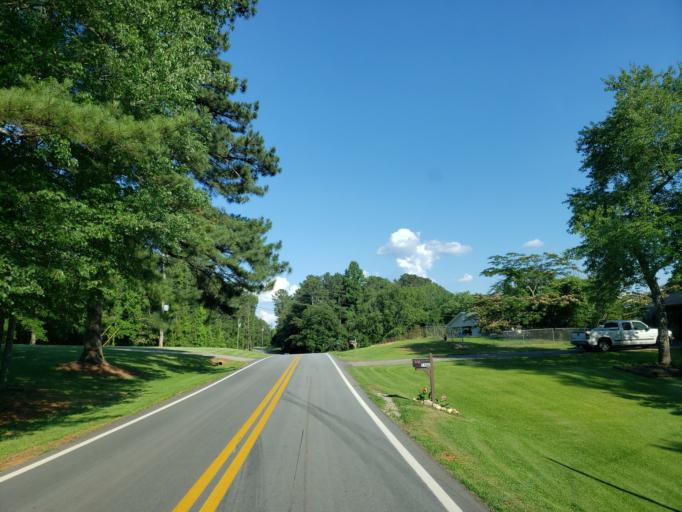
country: US
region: Georgia
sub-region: Haralson County
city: Bremen
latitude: 33.7066
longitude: -85.1124
